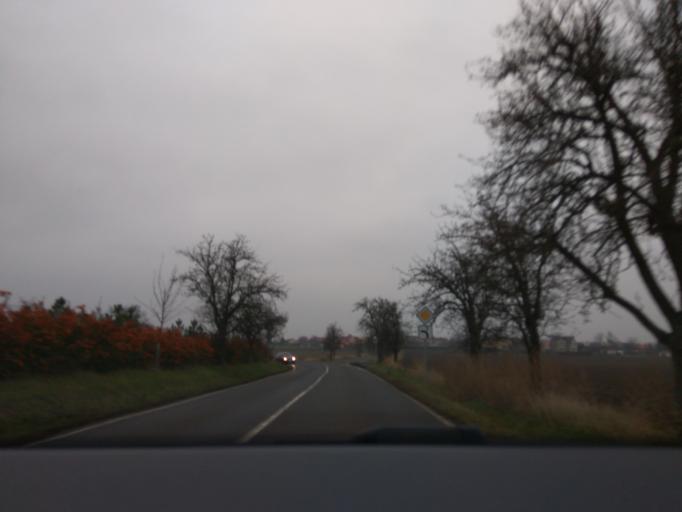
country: CZ
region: Praha
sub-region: Praha 19
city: Kbely
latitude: 50.1504
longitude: 14.5430
